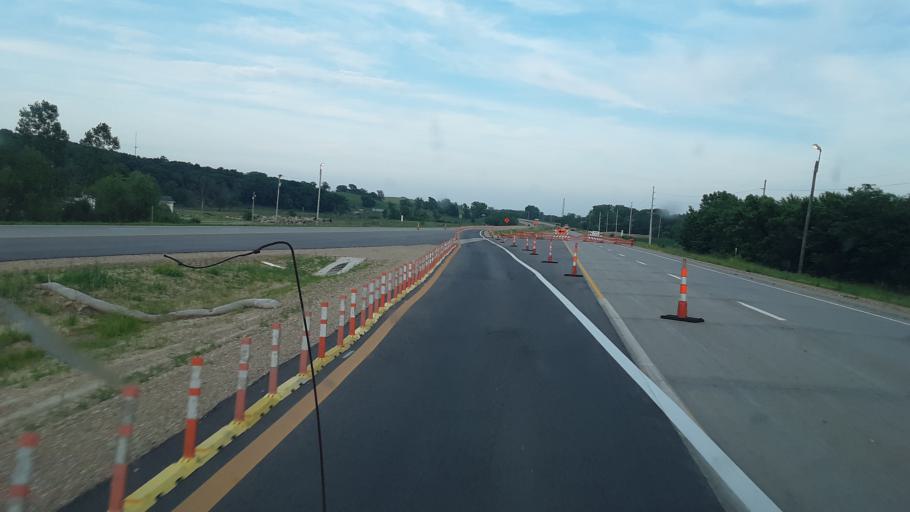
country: US
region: Iowa
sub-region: Tama County
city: Toledo
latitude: 42.0017
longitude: -92.7114
